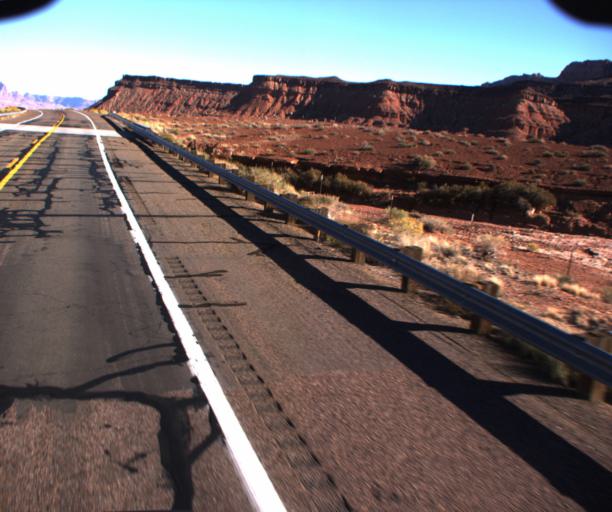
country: US
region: Arizona
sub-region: Coconino County
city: LeChee
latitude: 36.6939
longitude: -111.6547
